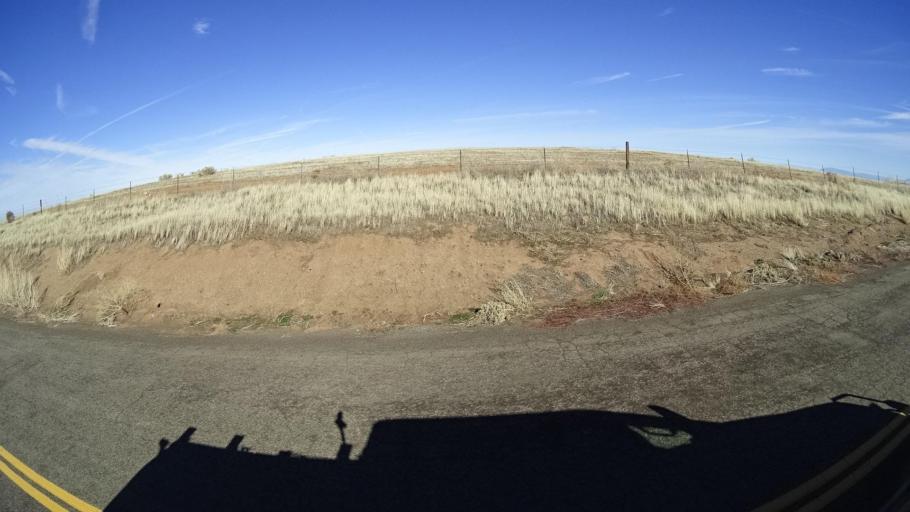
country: US
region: California
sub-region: Kern County
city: Maricopa
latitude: 34.9046
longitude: -119.3822
